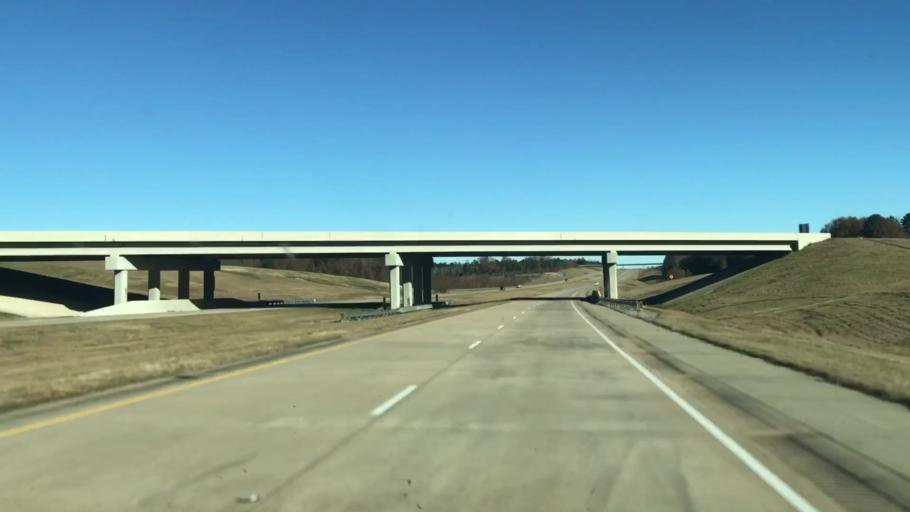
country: US
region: Louisiana
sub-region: Caddo Parish
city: Vivian
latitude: 32.9965
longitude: -93.9093
